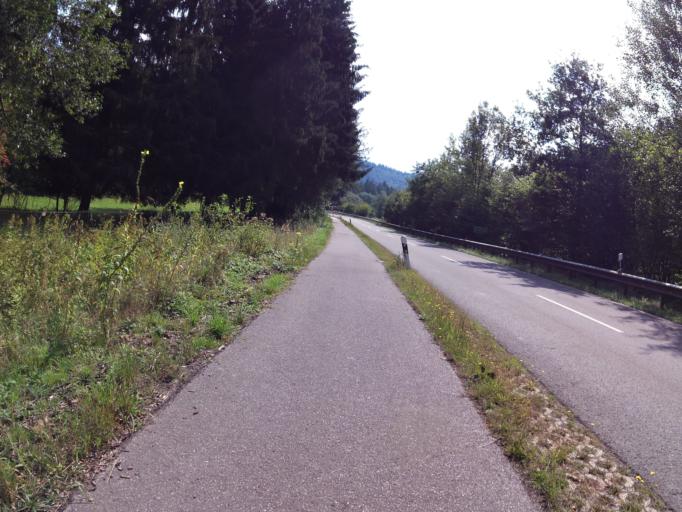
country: DE
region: Rheinland-Pfalz
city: Orenhofen
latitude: 49.8673
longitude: 6.6431
